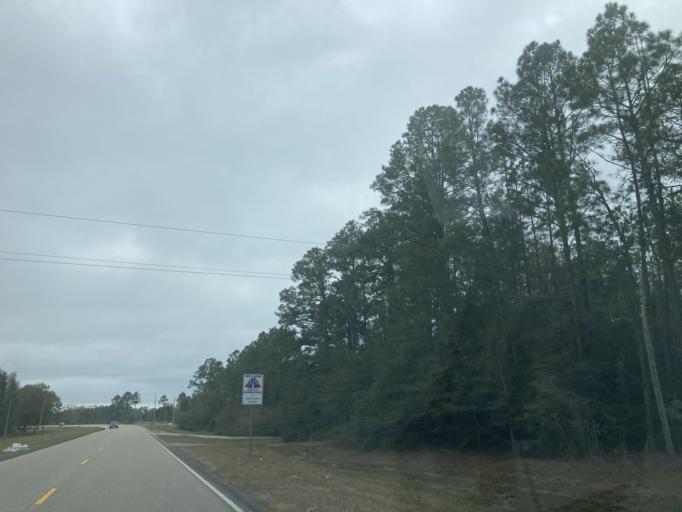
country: US
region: Mississippi
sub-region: Jackson County
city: Latimer
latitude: 30.5447
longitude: -88.9276
